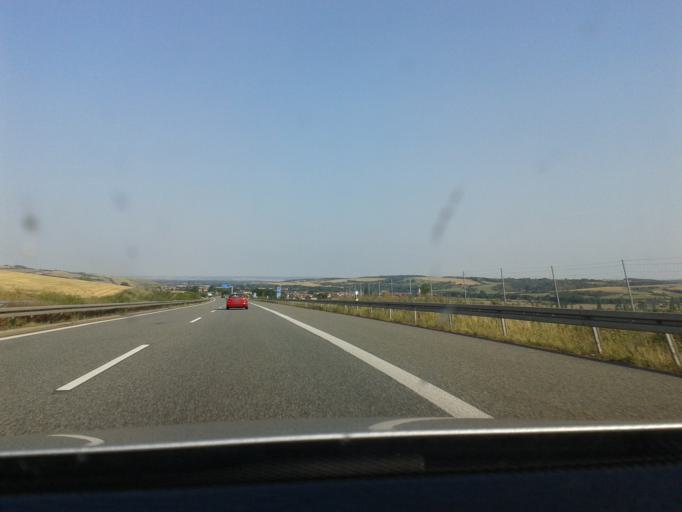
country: DE
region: Saxony-Anhalt
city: Rossla
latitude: 51.4715
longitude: 11.0892
